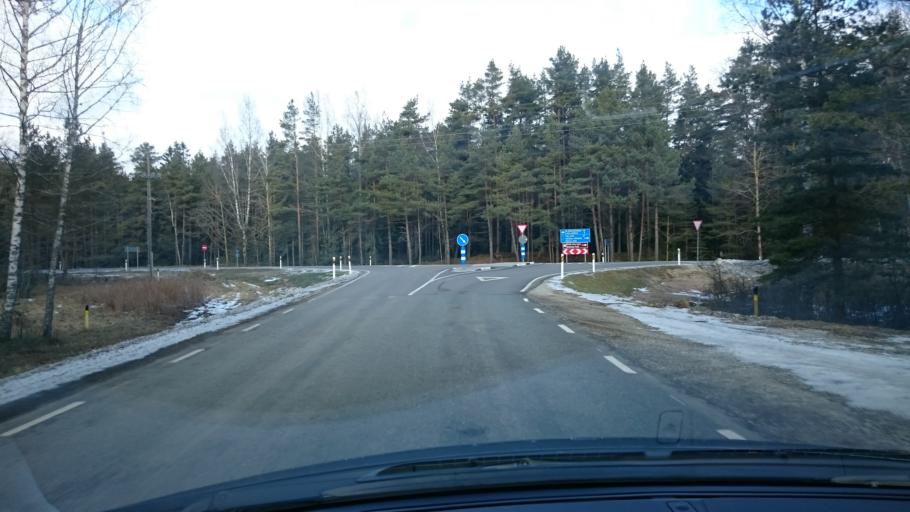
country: EE
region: Harju
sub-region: Keila linn
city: Keila
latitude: 59.3924
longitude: 24.2939
